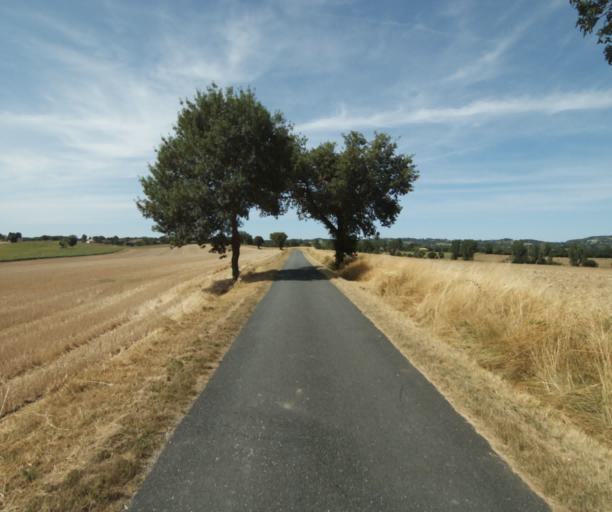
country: FR
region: Midi-Pyrenees
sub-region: Departement du Tarn
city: Puylaurens
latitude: 43.5277
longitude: 2.0230
